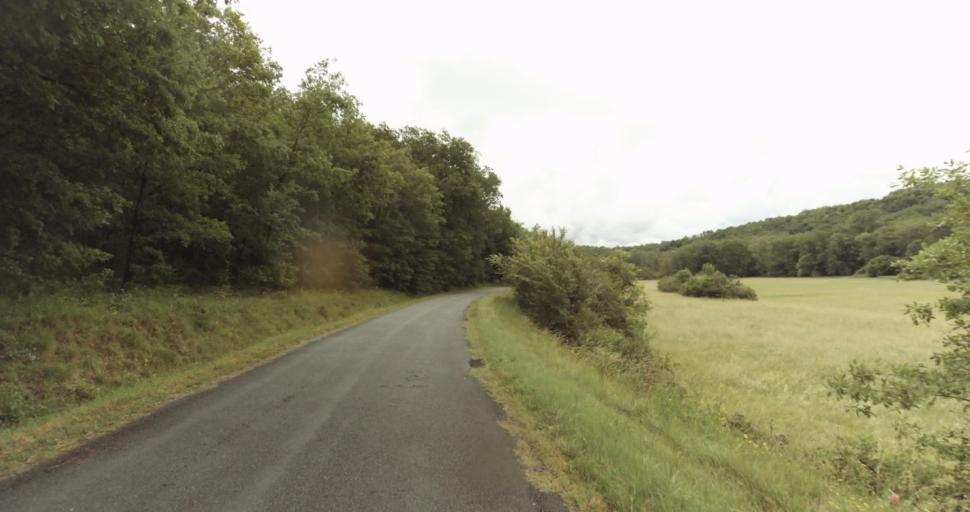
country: FR
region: Aquitaine
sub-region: Departement de la Dordogne
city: Beaumont-du-Perigord
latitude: 44.7537
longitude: 0.8207
